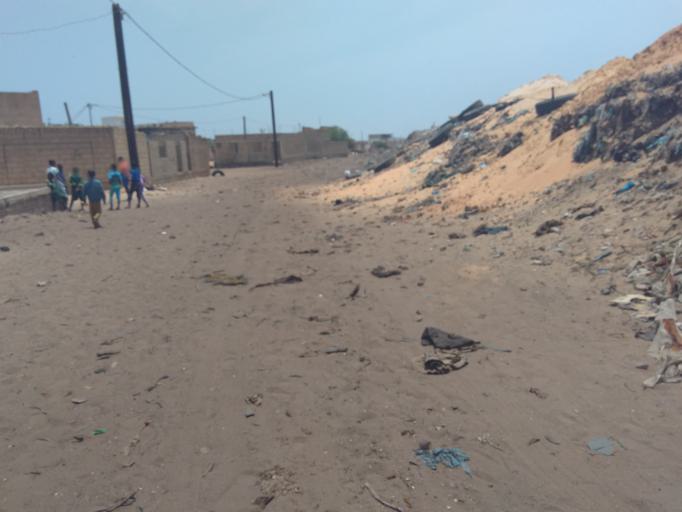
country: SN
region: Dakar
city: Pikine
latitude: 14.7935
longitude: -17.3260
